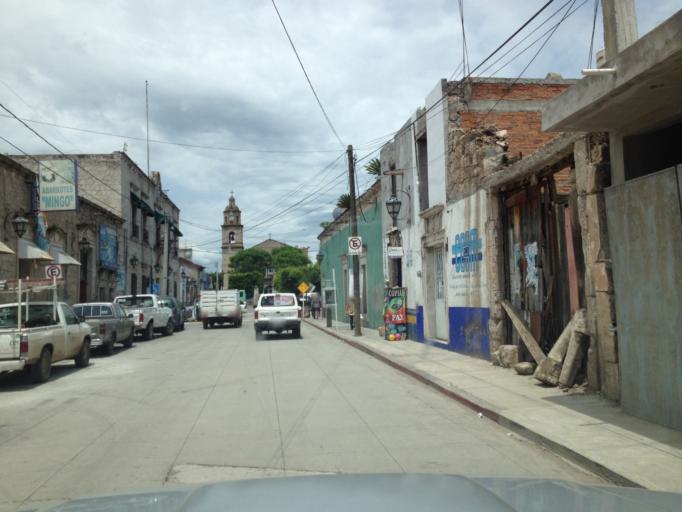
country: MX
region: Michoacan
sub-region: Tarimbaro
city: Meson Nuevo (Canada de la Magdalena)
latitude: 19.7955
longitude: -101.1770
